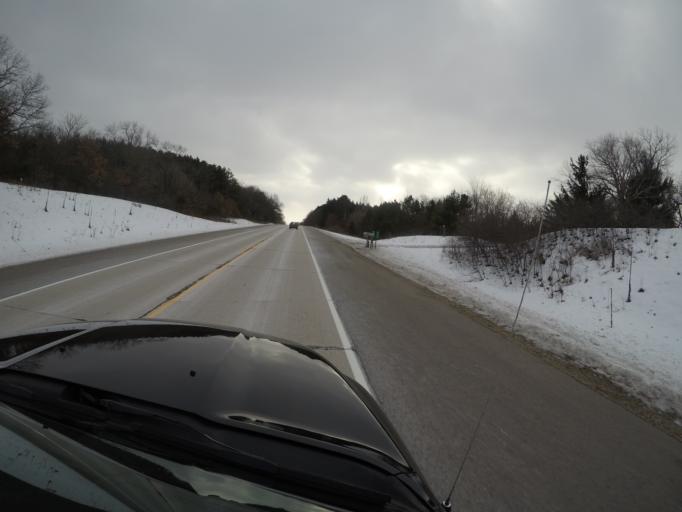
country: US
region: Wisconsin
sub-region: Trempealeau County
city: Galesville
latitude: 44.0570
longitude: -91.2912
